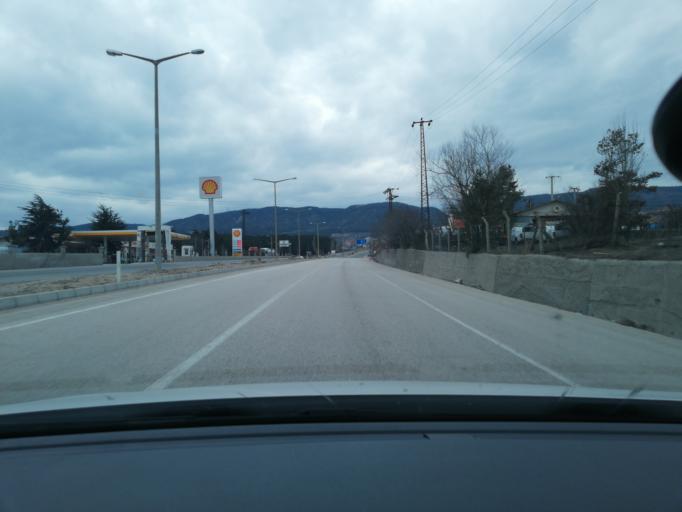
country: TR
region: Bolu
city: Gerede
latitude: 40.7863
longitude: 32.2100
